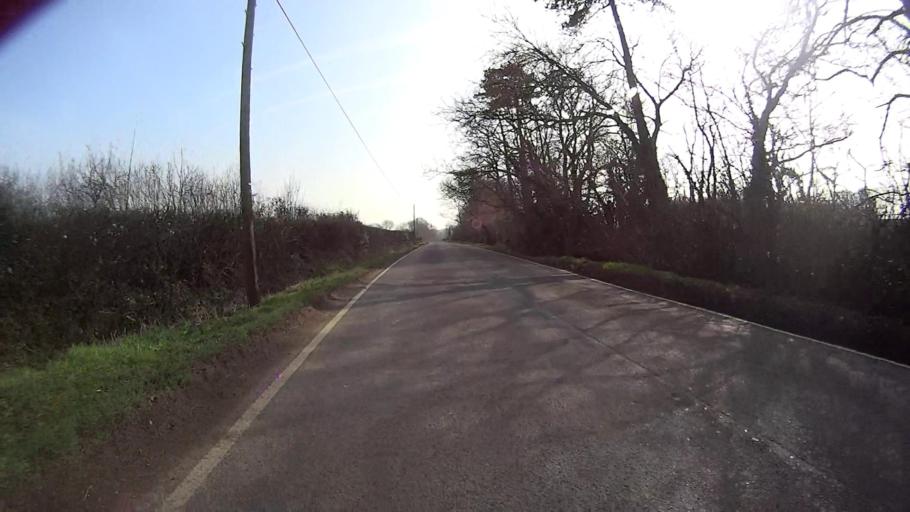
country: GB
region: England
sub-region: Surrey
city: Salfords
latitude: 51.2115
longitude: -0.1537
